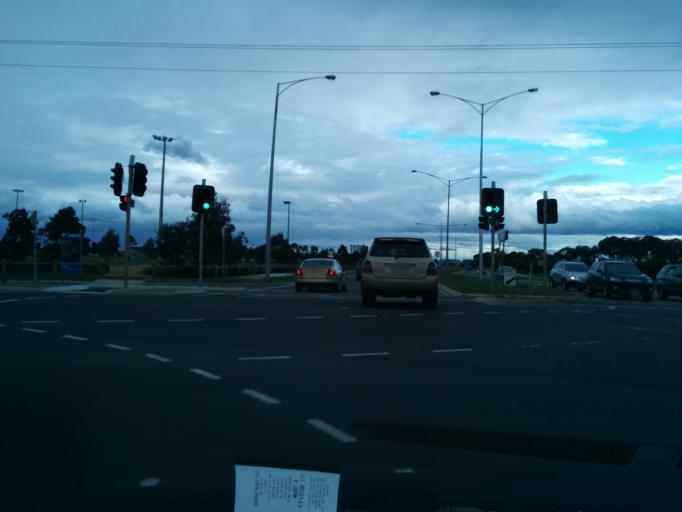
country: AU
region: Victoria
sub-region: Wyndham
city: Point Cook
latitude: -37.9099
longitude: 144.7517
